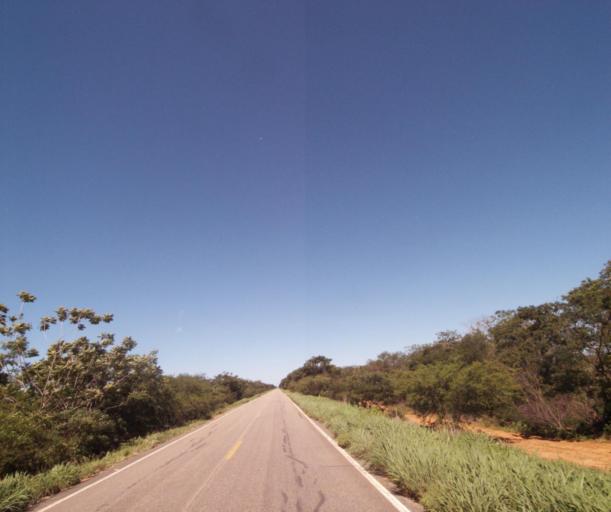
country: BR
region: Bahia
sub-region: Palmas De Monte Alto
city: Palmas de Monte Alto
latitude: -14.2619
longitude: -43.3152
